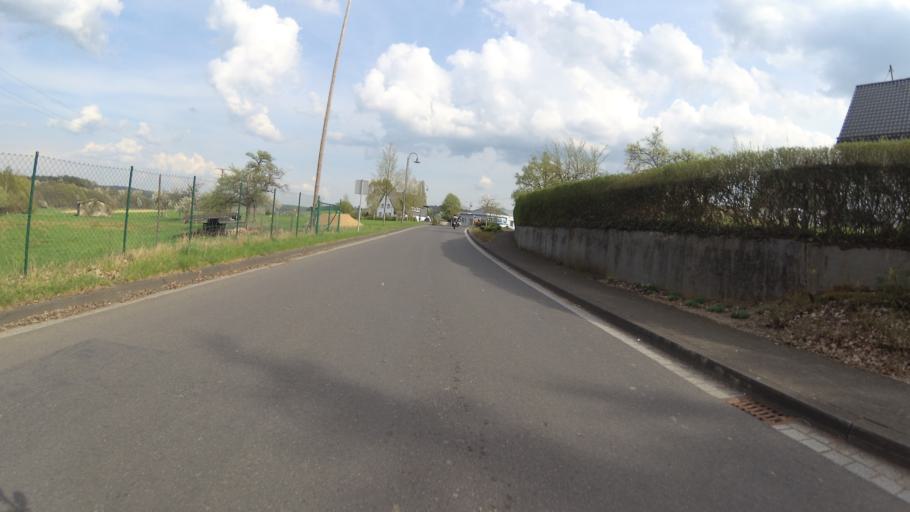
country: DE
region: Rheinland-Pfalz
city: Welcherath
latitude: 50.3194
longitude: 6.9661
